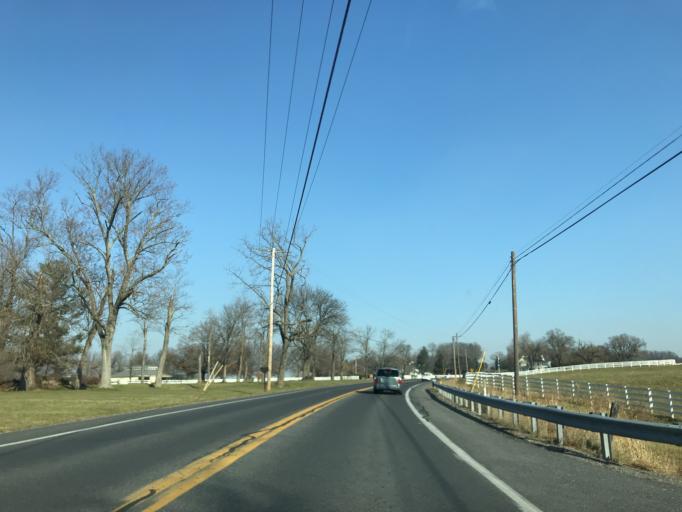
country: US
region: Pennsylvania
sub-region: York County
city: Pennville
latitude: 39.7670
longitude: -77.0258
